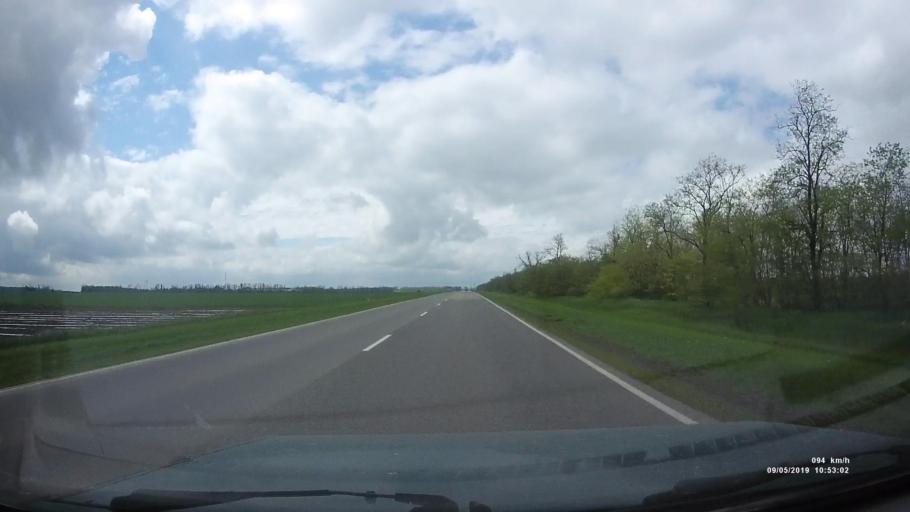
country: RU
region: Rostov
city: Peshkovo
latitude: 46.8937
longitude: 39.3466
